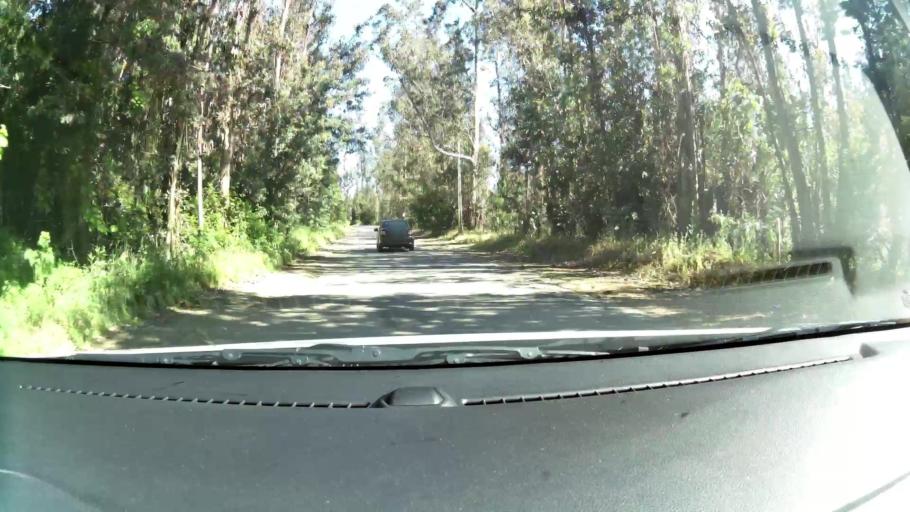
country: CL
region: Valparaiso
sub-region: Provincia de Valparaiso
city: Vina del Mar
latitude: -33.1520
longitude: -71.5599
